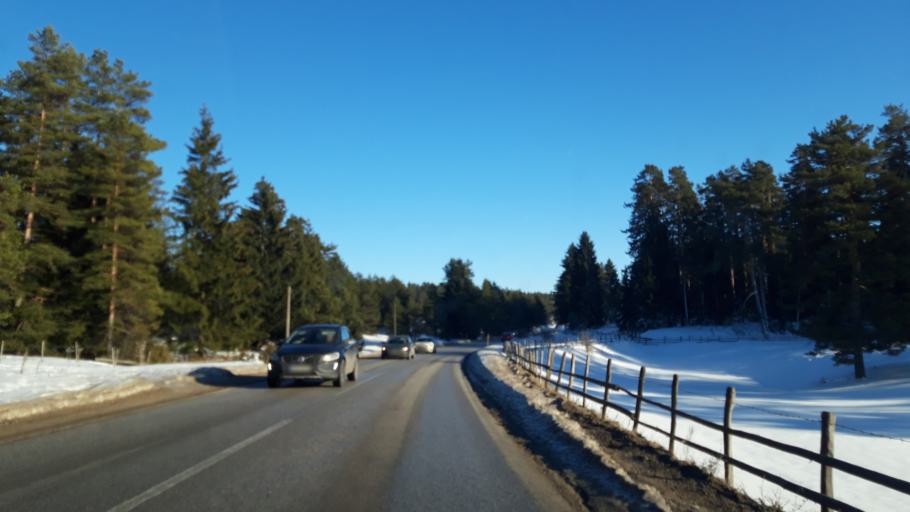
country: BA
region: Republika Srpska
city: Sokolac
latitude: 43.9192
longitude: 18.6921
